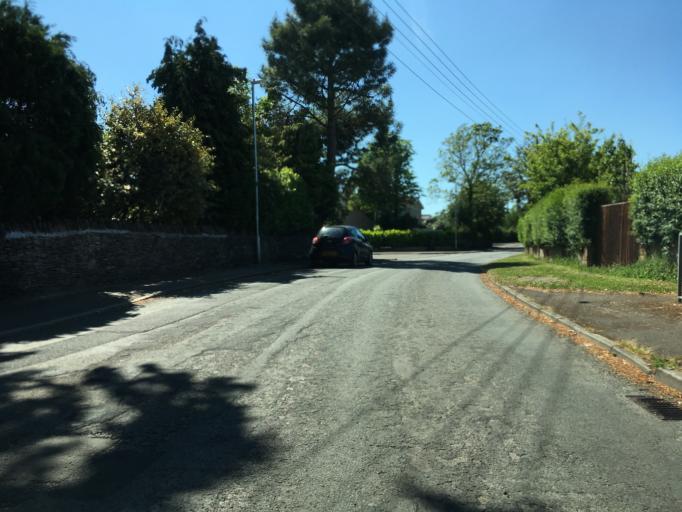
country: GB
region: England
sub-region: South Gloucestershire
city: Winterbourne
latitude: 51.5345
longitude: -2.4916
